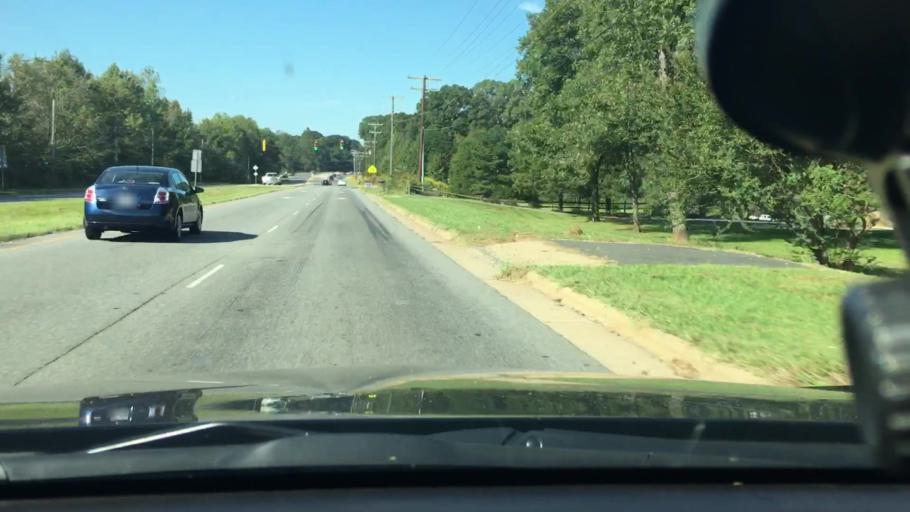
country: US
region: North Carolina
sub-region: Mecklenburg County
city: Mint Hill
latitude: 35.2242
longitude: -80.6194
